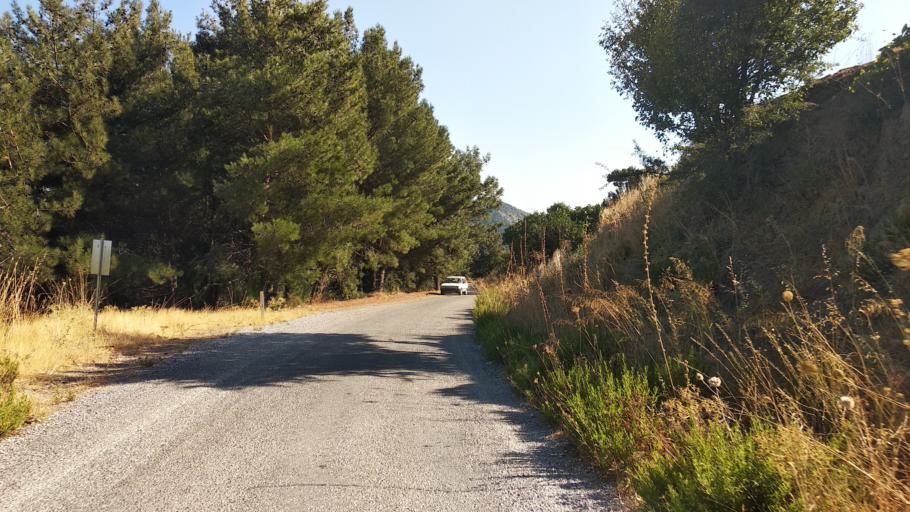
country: TR
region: Izmir
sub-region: Seferihisar
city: Seferhisar
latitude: 38.3277
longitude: 26.9423
